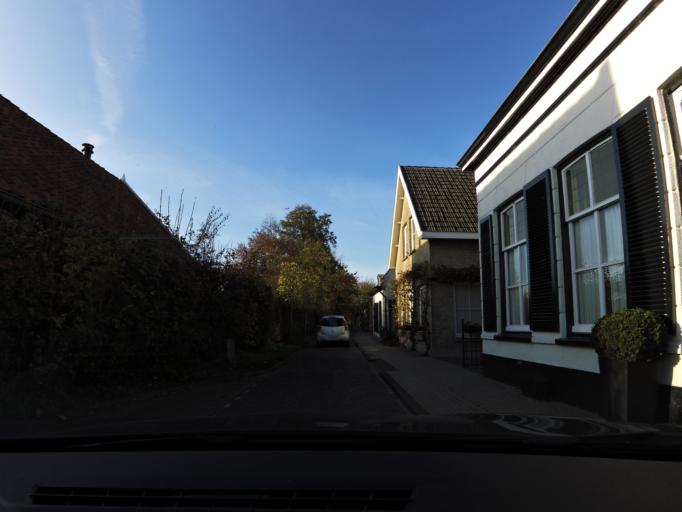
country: NL
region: North Brabant
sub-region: Gemeente Made en Drimmelen
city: Drimmelen
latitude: 51.7084
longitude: 4.8043
